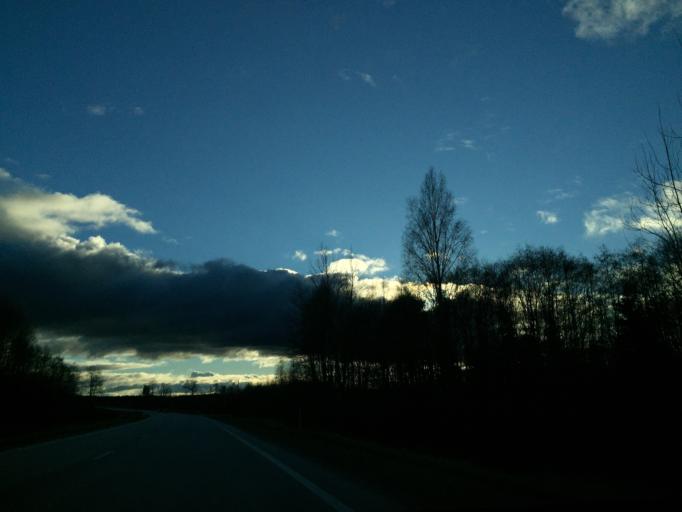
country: LV
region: Koceni
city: Koceni
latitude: 57.5343
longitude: 25.3704
